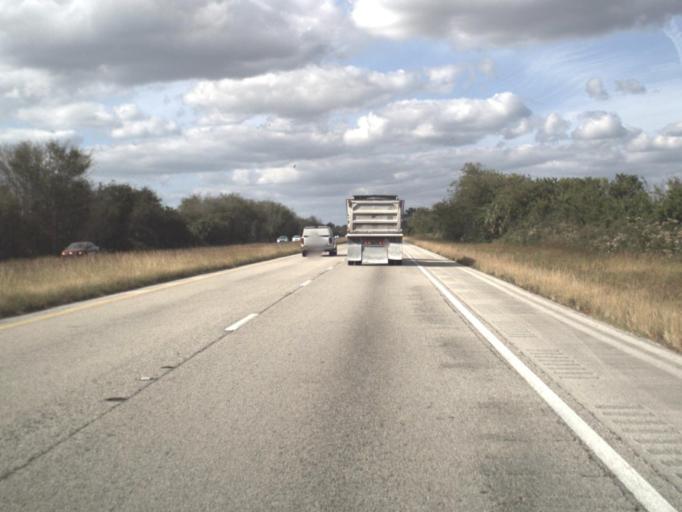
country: US
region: Florida
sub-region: Brevard County
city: Port Saint John
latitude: 28.4374
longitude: -80.8607
